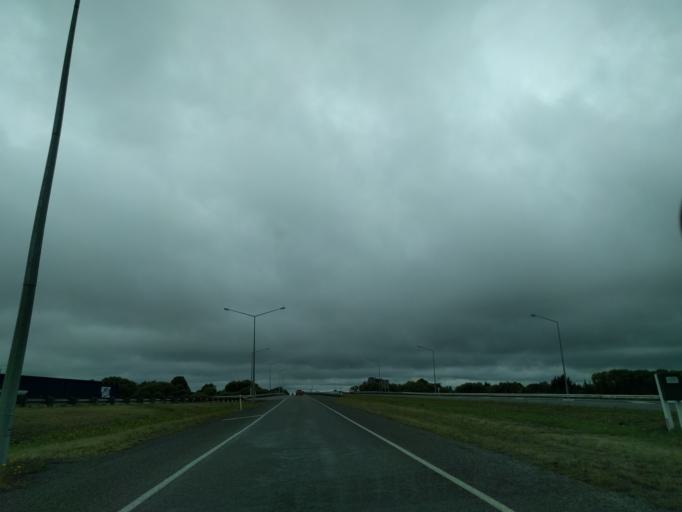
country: NZ
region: Canterbury
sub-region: Waimakariri District
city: Kaiapoi
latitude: -43.3756
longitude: 172.6463
